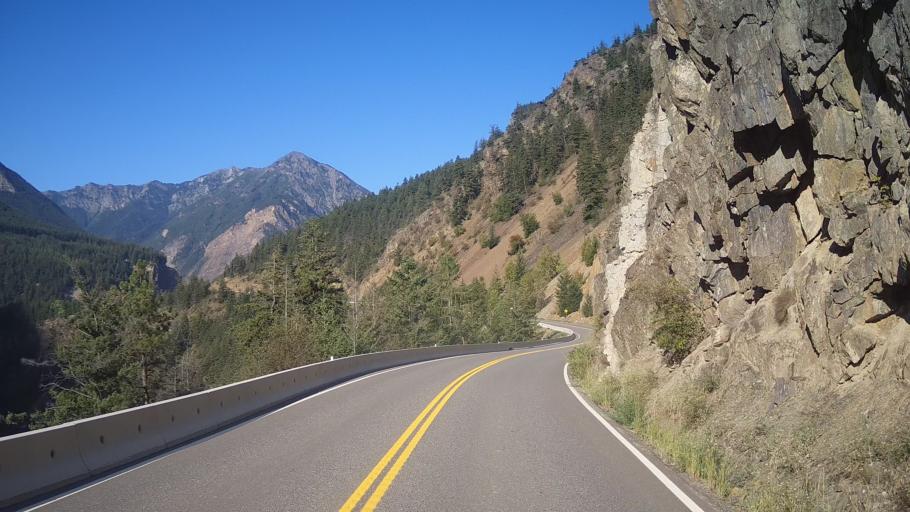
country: CA
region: British Columbia
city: Lillooet
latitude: 50.6582
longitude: -121.9943
